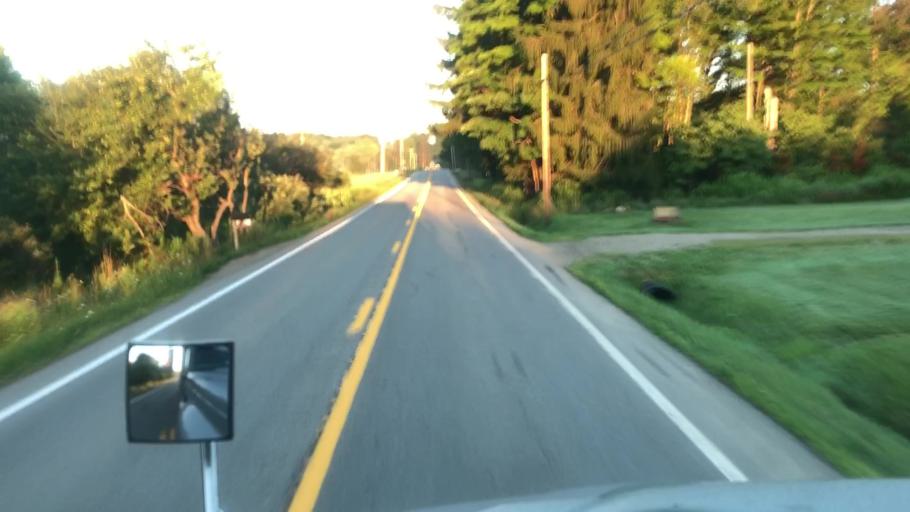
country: US
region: Pennsylvania
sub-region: Crawford County
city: Titusville
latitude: 41.5946
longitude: -79.5993
